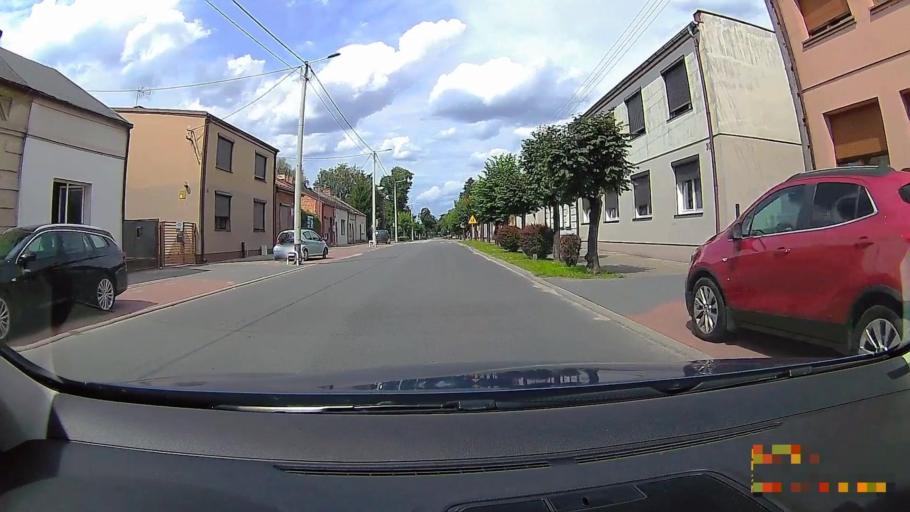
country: PL
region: Greater Poland Voivodeship
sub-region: Powiat koninski
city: Rychwal
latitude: 52.0720
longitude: 18.1647
